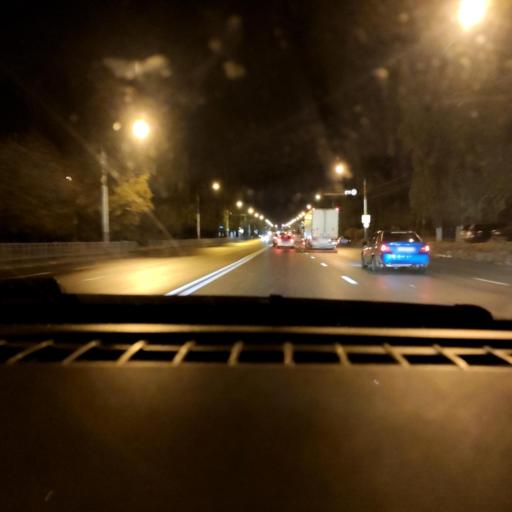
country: RU
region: Voronezj
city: Maslovka
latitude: 51.6095
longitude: 39.2370
